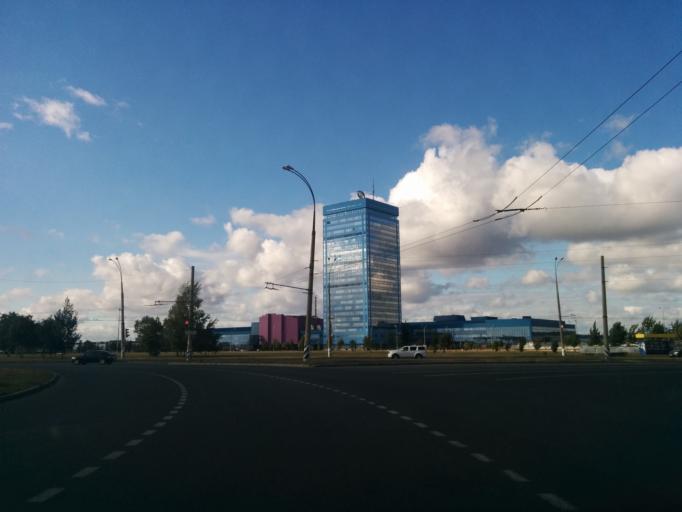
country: RU
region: Samara
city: Tol'yatti
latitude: 53.5526
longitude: 49.2680
